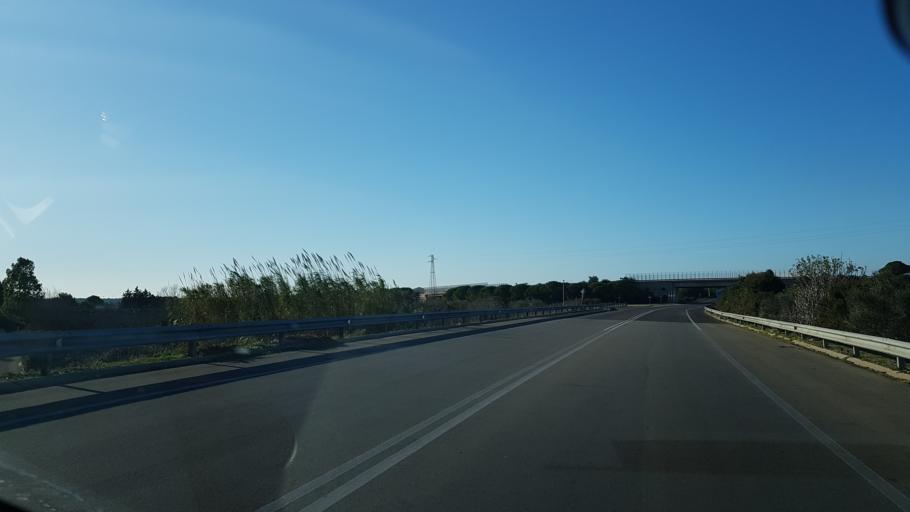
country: IT
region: Apulia
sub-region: Provincia di Lecce
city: Taviano
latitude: 39.9995
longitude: 18.0690
